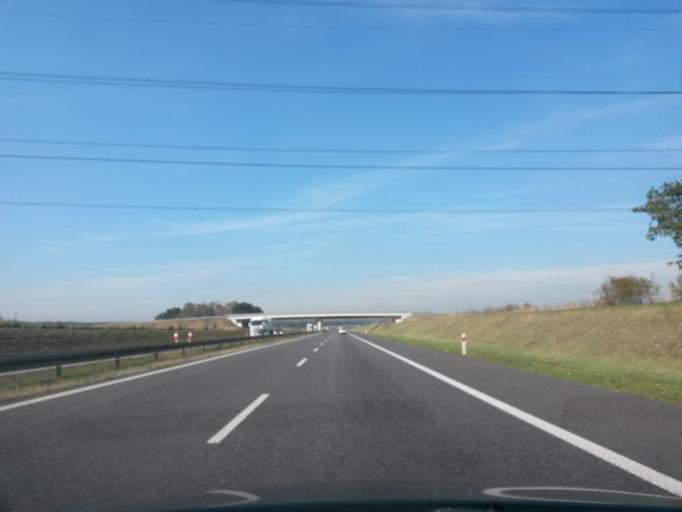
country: PL
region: Silesian Voivodeship
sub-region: Powiat gliwicki
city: Sosnicowice
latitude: 50.2906
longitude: 18.5630
